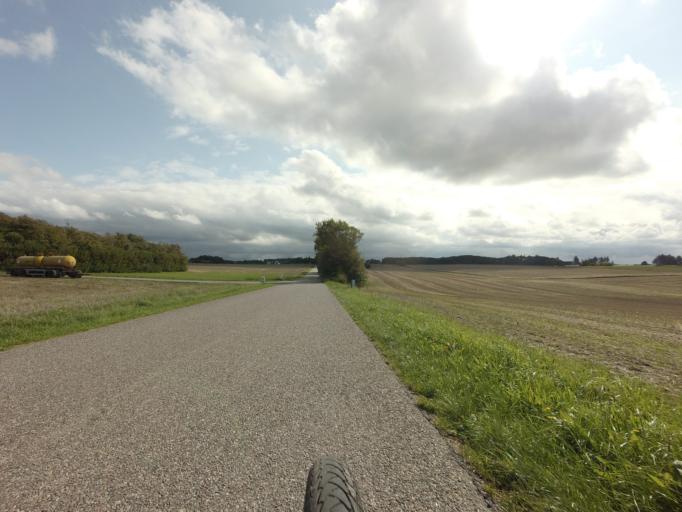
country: DK
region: North Denmark
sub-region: Hjorring Kommune
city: Hjorring
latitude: 57.5236
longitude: 10.0466
